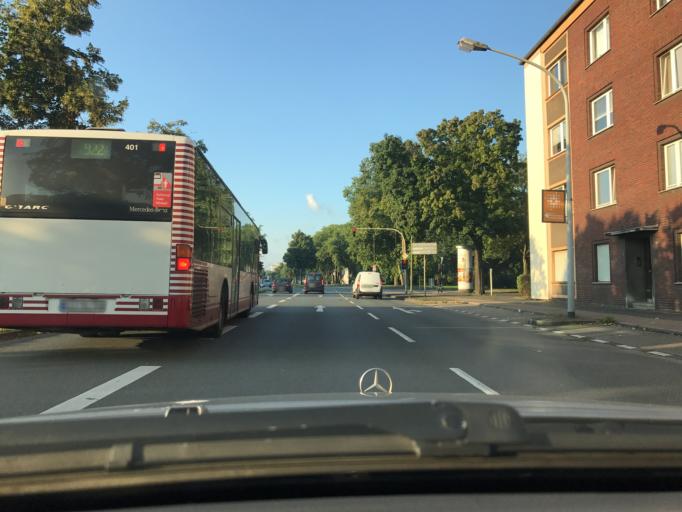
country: DE
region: North Rhine-Westphalia
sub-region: Regierungsbezirk Dusseldorf
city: Hochfeld
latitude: 51.4052
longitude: 6.7116
